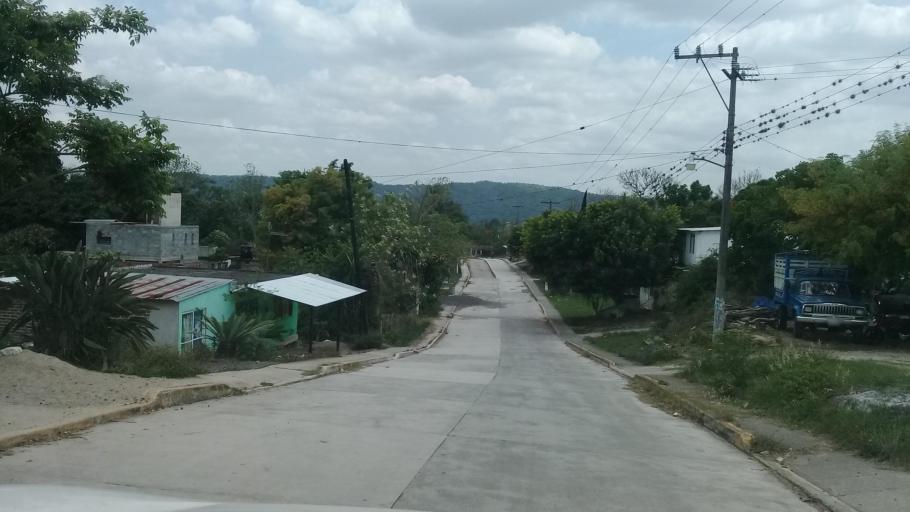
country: MX
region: Veracruz
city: Jalcomulco
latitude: 19.3926
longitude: -96.7893
